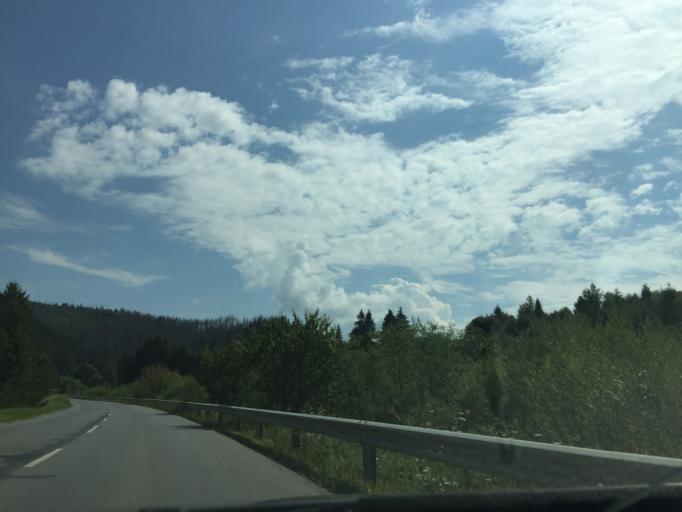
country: SK
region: Zilinsky
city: Namestovo
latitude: 49.3839
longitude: 19.3798
